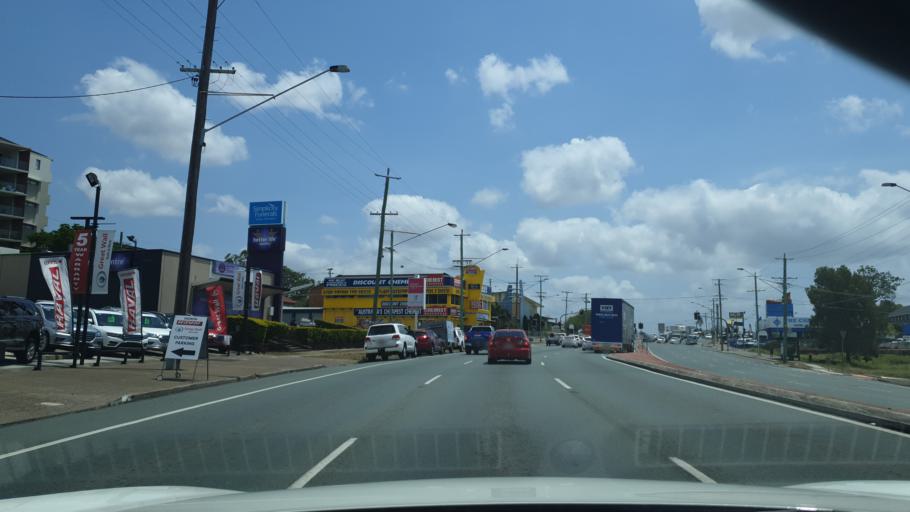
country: AU
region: Queensland
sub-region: Brisbane
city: Wavell Heights
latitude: -27.3949
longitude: 153.0308
